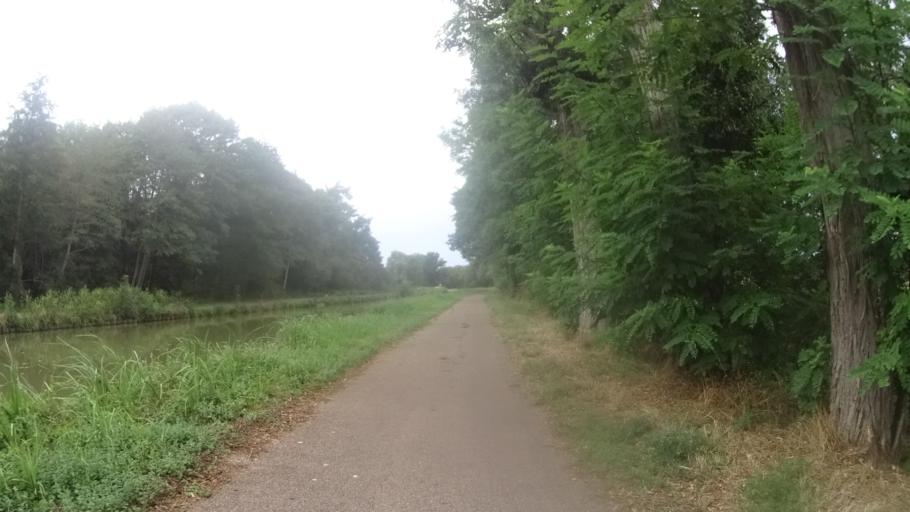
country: FR
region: Bourgogne
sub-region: Departement de la Nievre
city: Imphy
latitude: 46.9288
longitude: 3.2254
